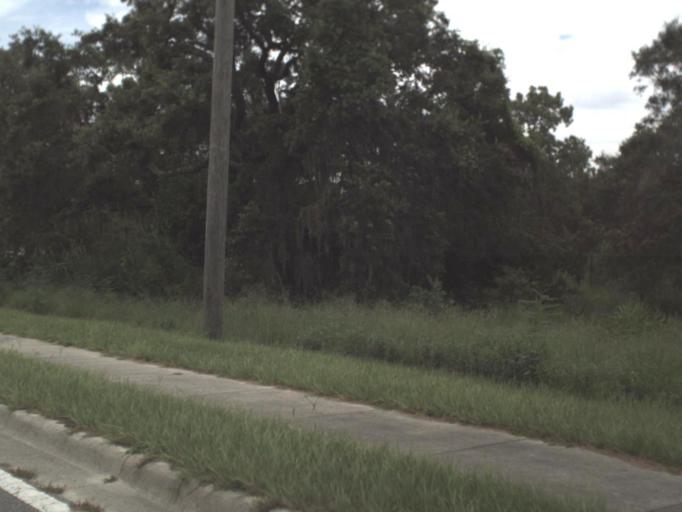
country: US
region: Florida
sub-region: Citrus County
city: Lecanto
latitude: 28.8756
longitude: -82.5199
